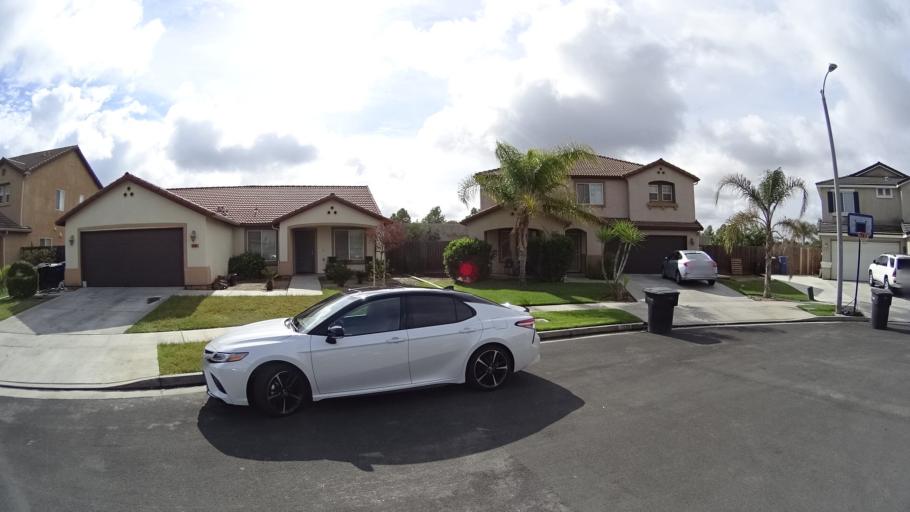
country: US
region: California
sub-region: Kings County
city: Lucerne
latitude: 36.3536
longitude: -119.6653
